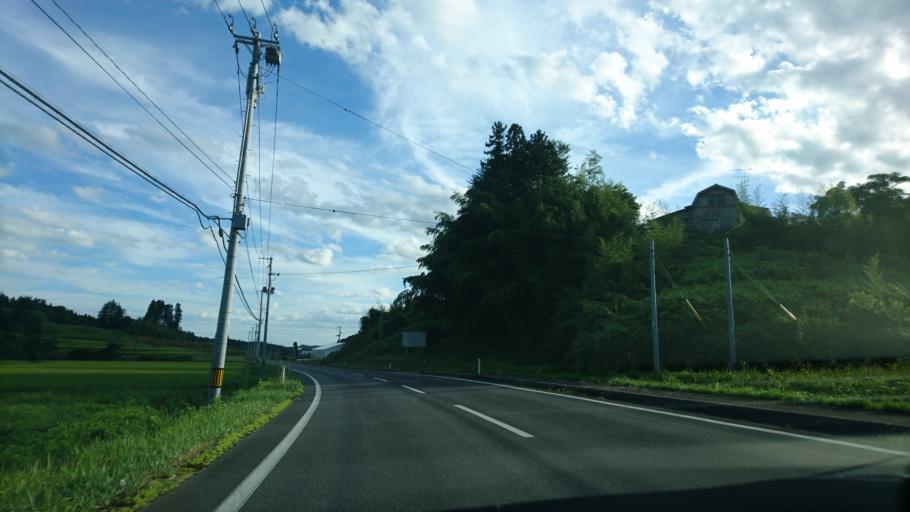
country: JP
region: Iwate
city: Ichinoseki
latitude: 38.8642
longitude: 141.1862
